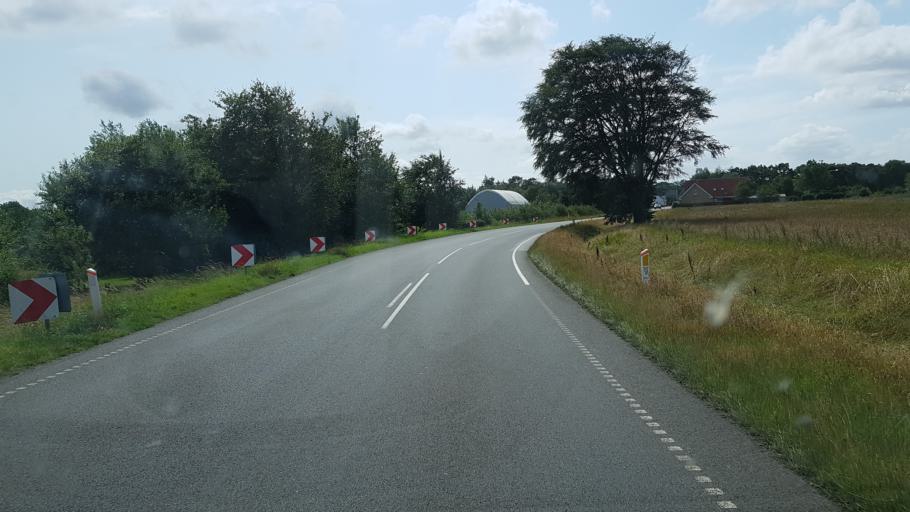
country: DK
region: South Denmark
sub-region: Vejen Kommune
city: Vejen
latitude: 55.5757
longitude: 9.1546
